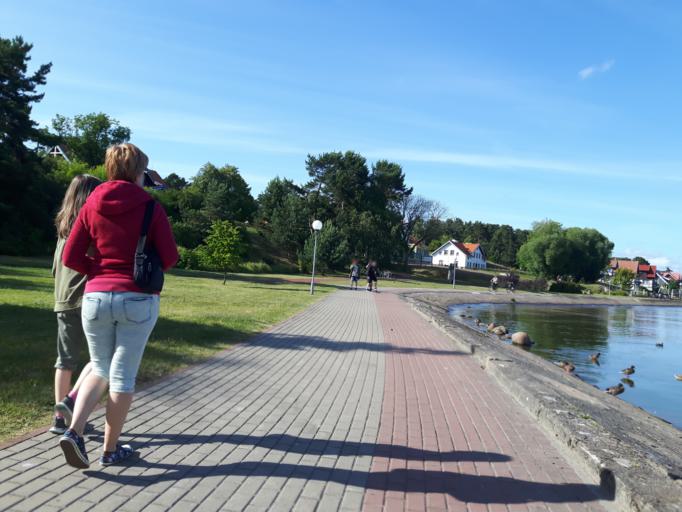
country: LT
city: Nida
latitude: 55.3138
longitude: 21.0151
